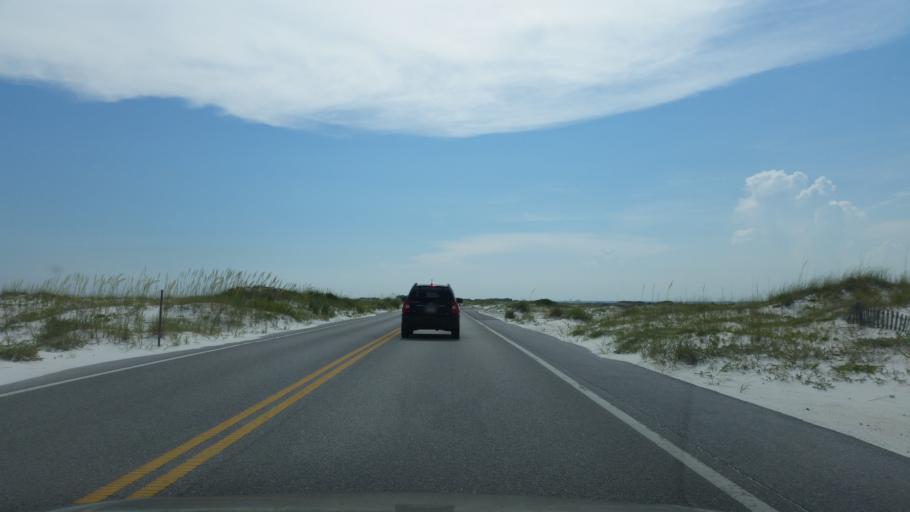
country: US
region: Florida
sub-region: Santa Rosa County
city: Woodlawn Beach
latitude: 30.3575
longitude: -87.0014
